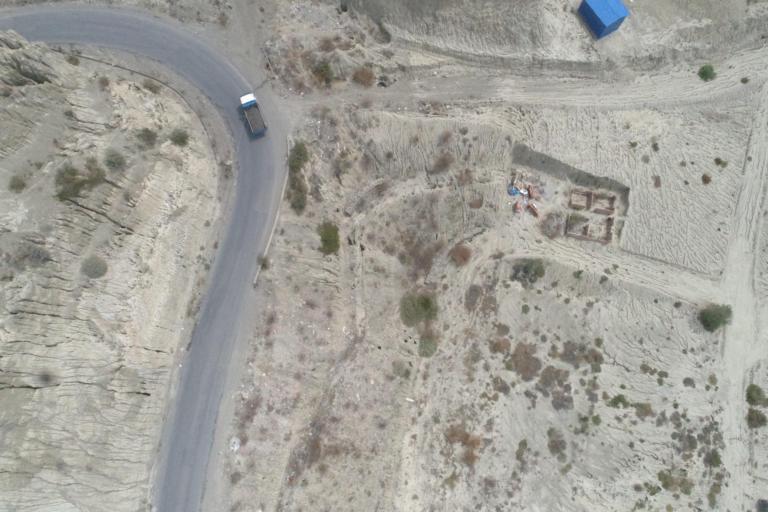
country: BO
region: La Paz
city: La Paz
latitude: -16.6027
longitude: -68.0688
